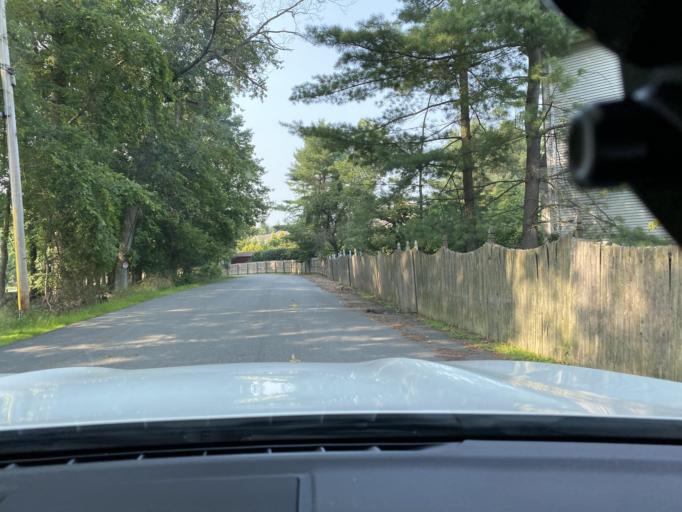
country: US
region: New York
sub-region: Rockland County
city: Airmont
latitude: 41.0817
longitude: -74.1203
